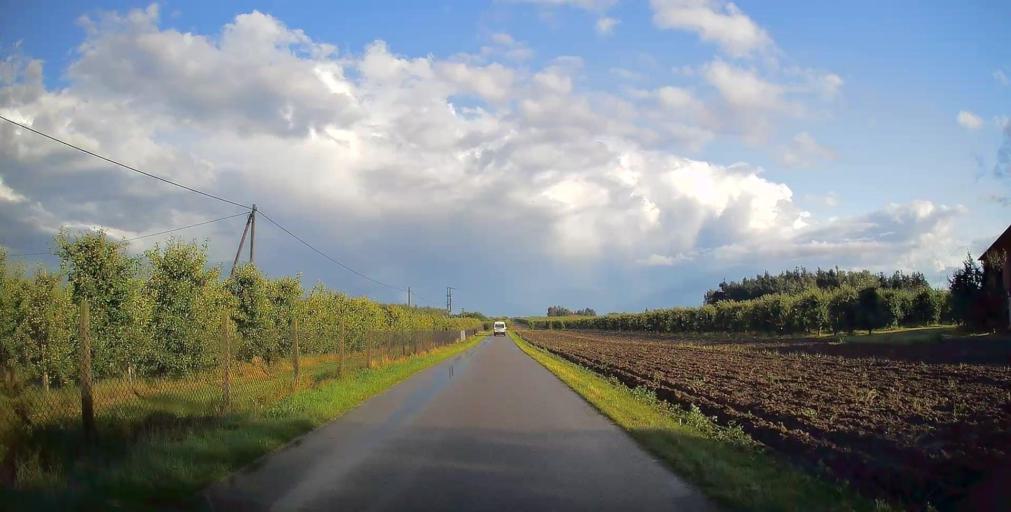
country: PL
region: Masovian Voivodeship
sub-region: Powiat grojecki
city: Goszczyn
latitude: 51.7505
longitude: 20.8852
